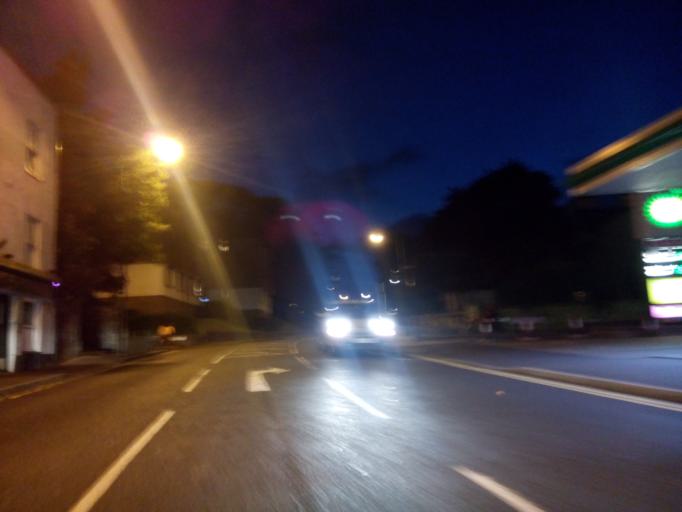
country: GB
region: England
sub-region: Kent
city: Dover
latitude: 51.1259
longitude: 1.3087
